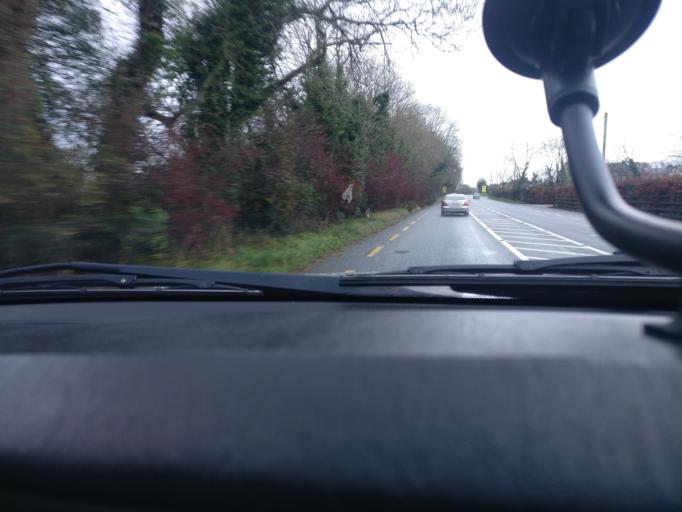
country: IE
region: Leinster
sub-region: Kildare
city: Kilcock
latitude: 53.4187
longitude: -6.7310
